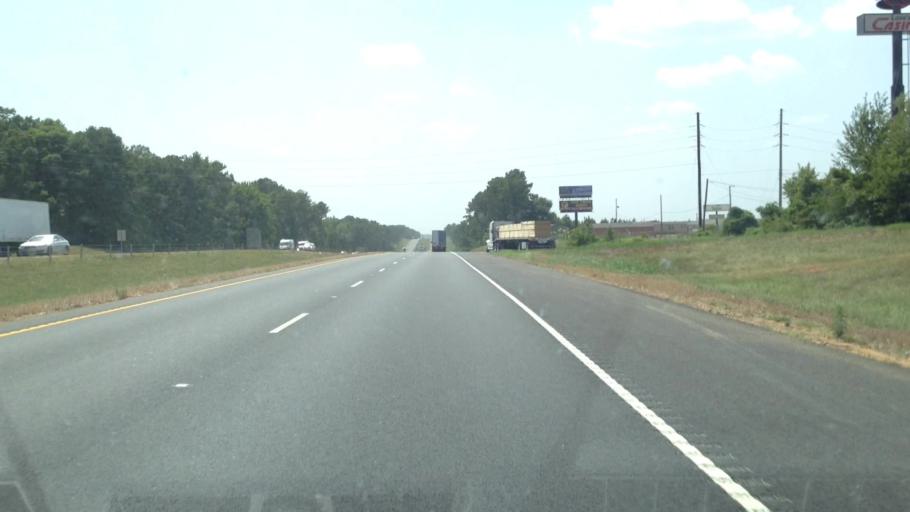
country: US
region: Louisiana
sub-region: Webster Parish
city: Minden
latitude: 32.5810
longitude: -93.2500
